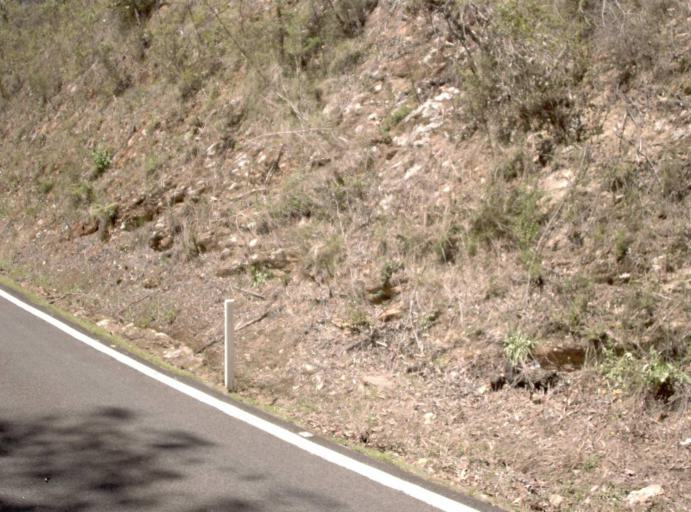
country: AU
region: New South Wales
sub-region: Bombala
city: Bombala
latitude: -37.5842
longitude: 148.9189
